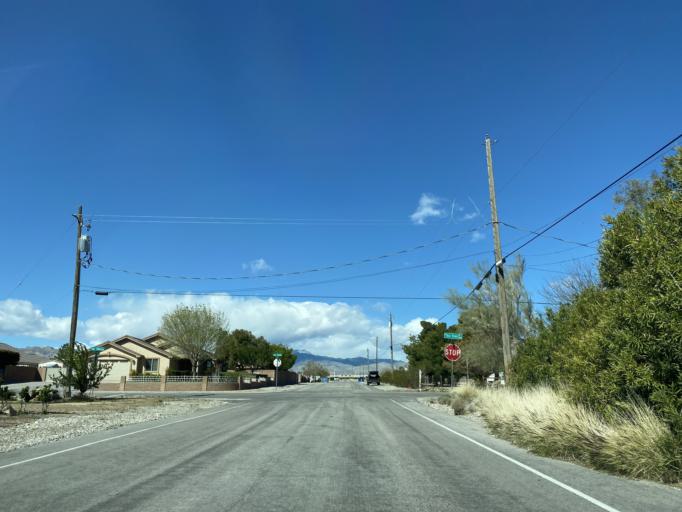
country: US
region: Nevada
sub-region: Clark County
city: North Las Vegas
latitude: 36.3320
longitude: -115.2847
